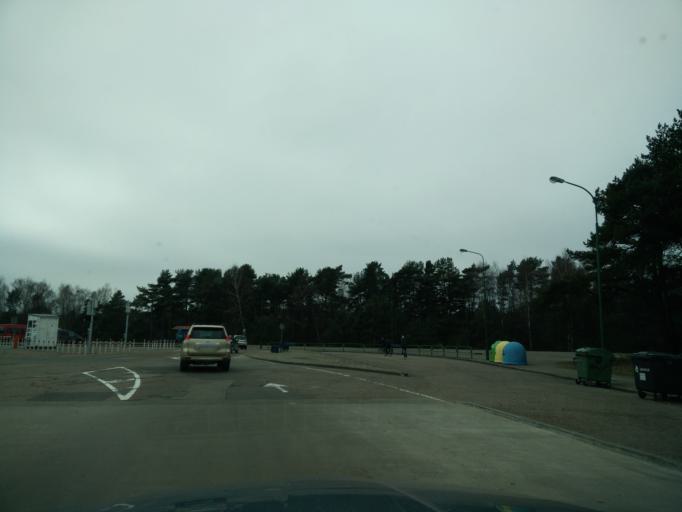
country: LT
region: Klaipedos apskritis
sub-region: Klaipeda
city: Klaipeda
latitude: 55.6857
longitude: 21.1303
